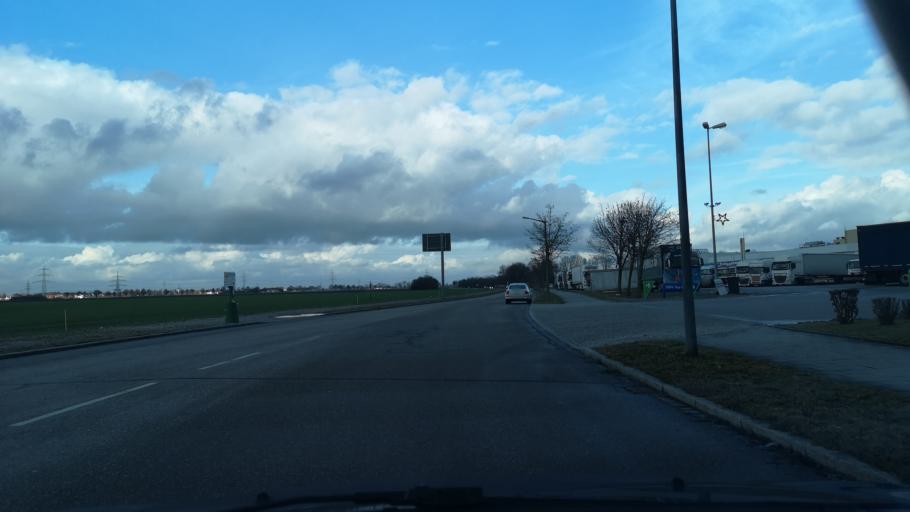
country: DE
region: Bavaria
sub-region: Upper Bavaria
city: Poing
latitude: 48.1687
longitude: 11.7917
